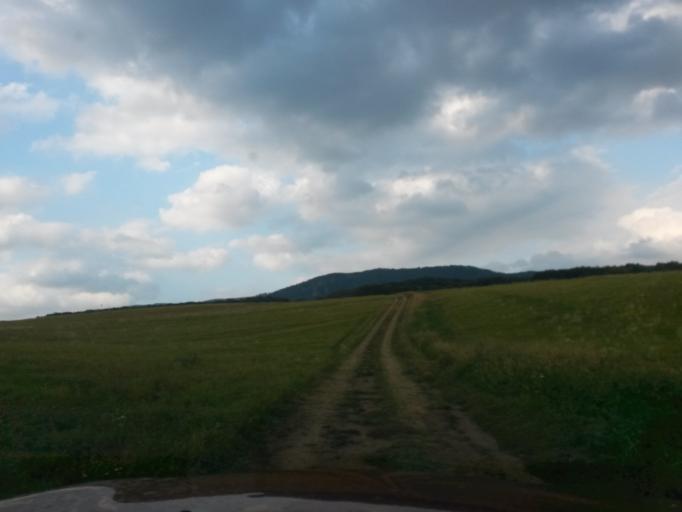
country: SK
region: Kosicky
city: Secovce
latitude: 48.8069
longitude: 21.4737
